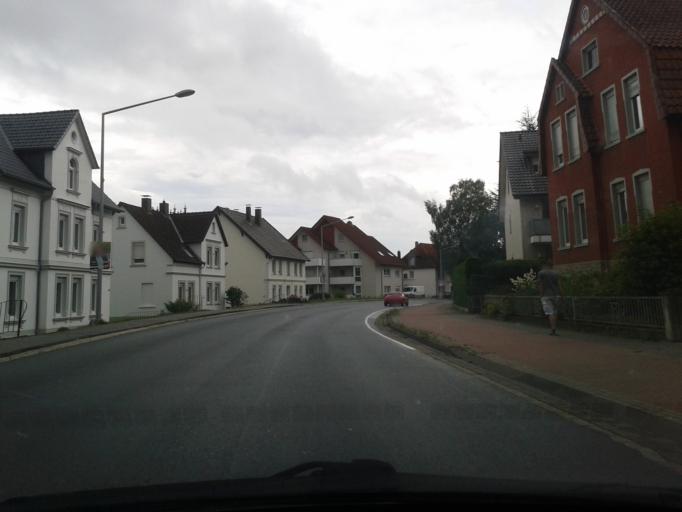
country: DE
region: North Rhine-Westphalia
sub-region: Regierungsbezirk Detmold
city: Detmold
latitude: 51.9237
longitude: 8.8985
